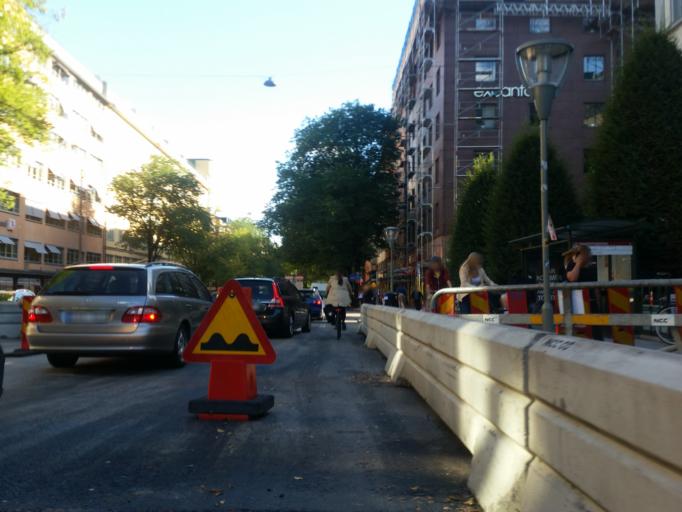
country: SE
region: Stockholm
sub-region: Stockholms Kommun
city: Stockholm
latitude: 59.3419
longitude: 18.0576
